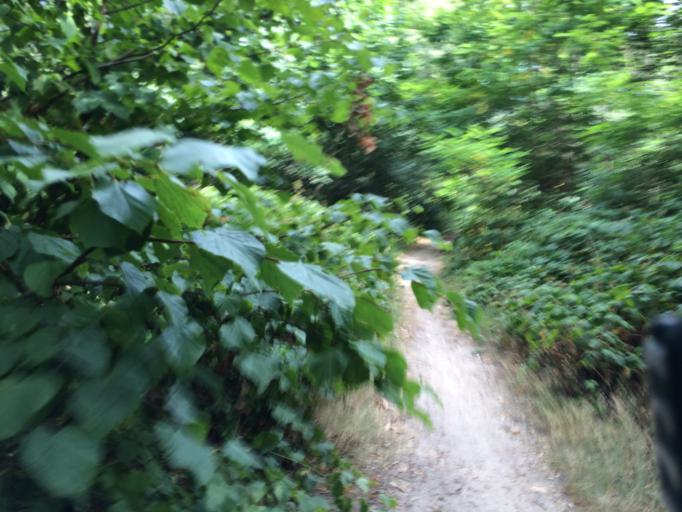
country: FR
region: Ile-de-France
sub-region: Departement de l'Essonne
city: Draveil
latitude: 48.6792
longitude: 2.4370
